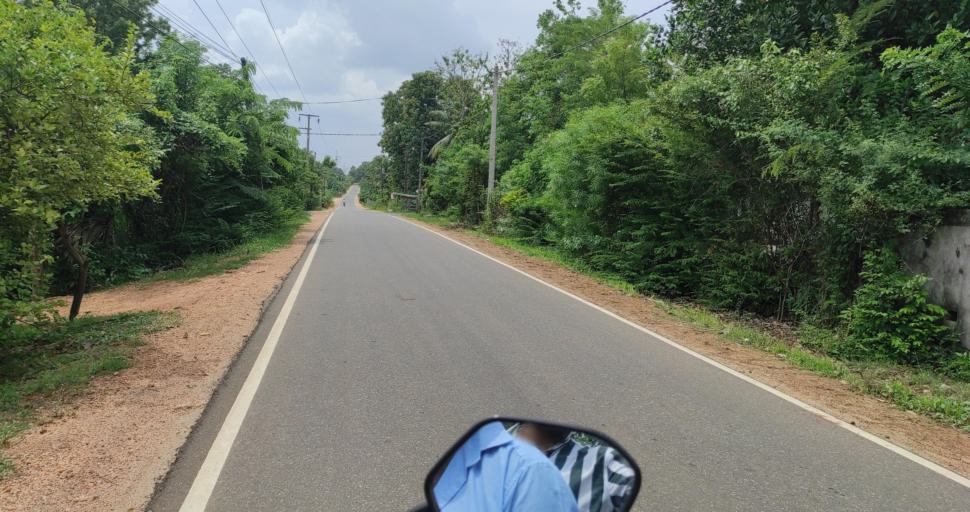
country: LK
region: Eastern Province
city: Trincomalee
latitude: 8.3753
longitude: 81.0133
